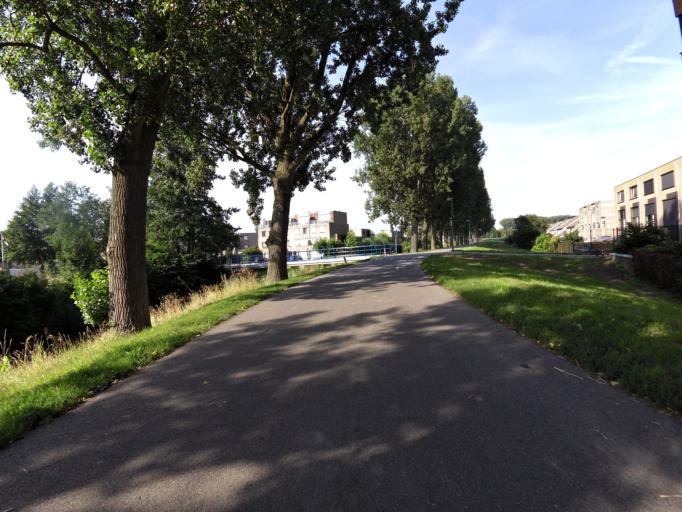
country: NL
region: South Holland
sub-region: Gemeente Papendrecht
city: Papendrecht
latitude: 51.8039
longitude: 4.7153
